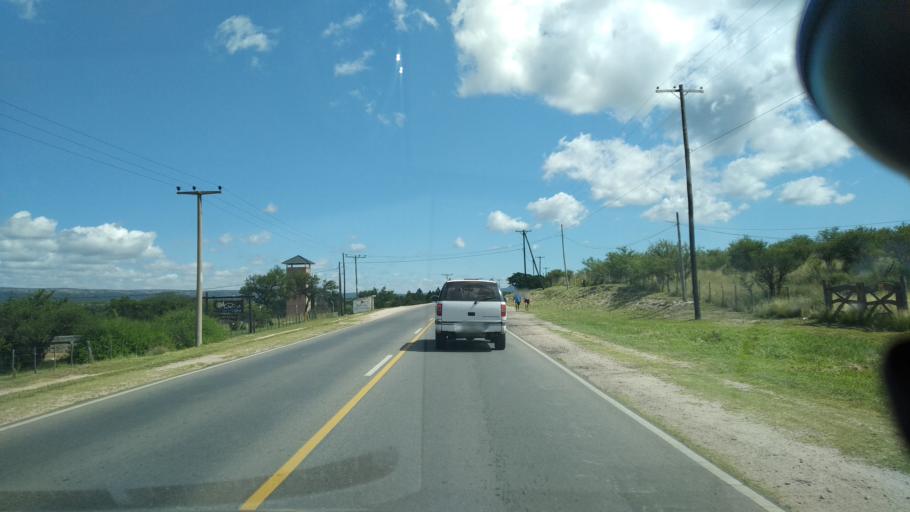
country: AR
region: Cordoba
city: Mina Clavero
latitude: -31.7784
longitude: -65.0002
